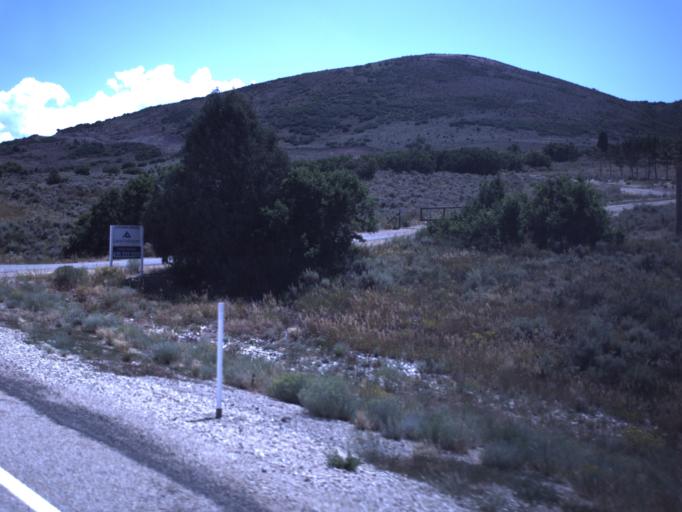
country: US
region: Utah
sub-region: Summit County
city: Francis
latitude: 40.5961
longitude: -111.3557
